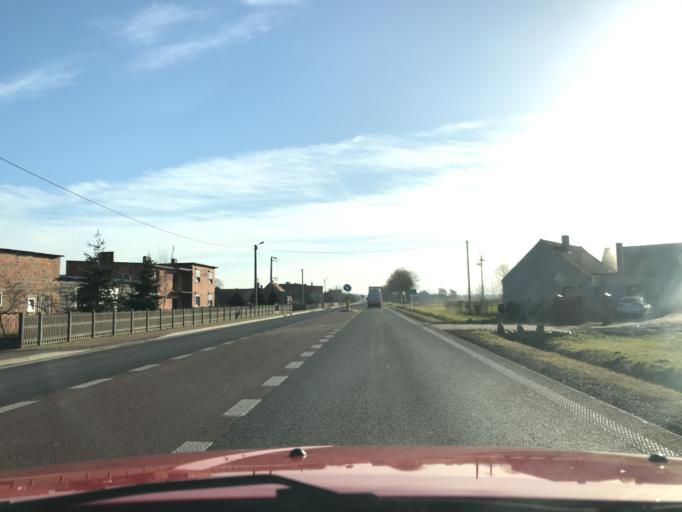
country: PL
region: Greater Poland Voivodeship
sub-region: Powiat pleszewski
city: Goluchow
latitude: 51.8706
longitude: 17.8945
